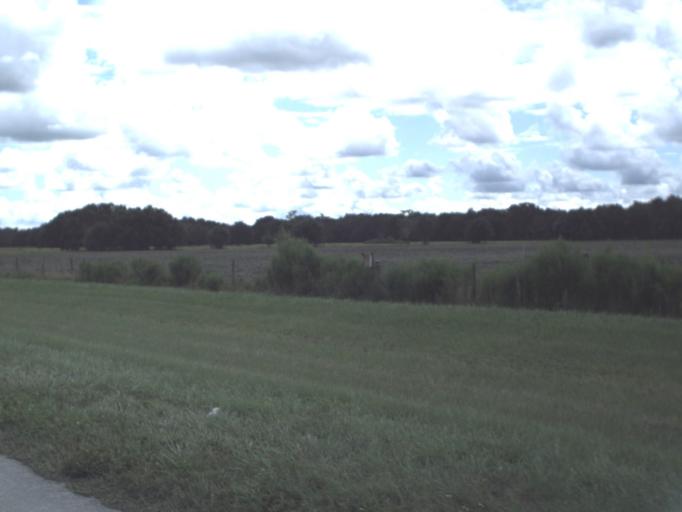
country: US
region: Florida
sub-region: DeSoto County
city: Southeast Arcadia
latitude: 27.2088
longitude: -81.8185
